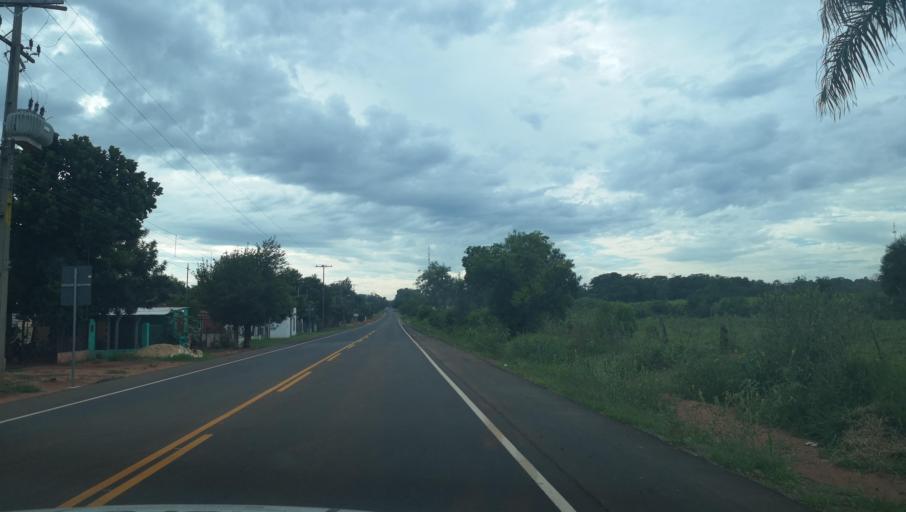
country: PY
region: San Pedro
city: Capiibary
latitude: -24.7431
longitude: -56.0351
